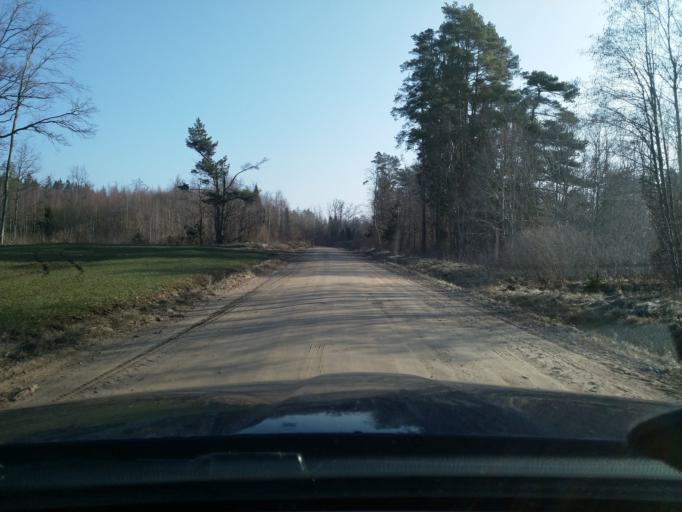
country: LV
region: Kuldigas Rajons
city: Kuldiga
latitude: 56.8654
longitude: 21.9078
